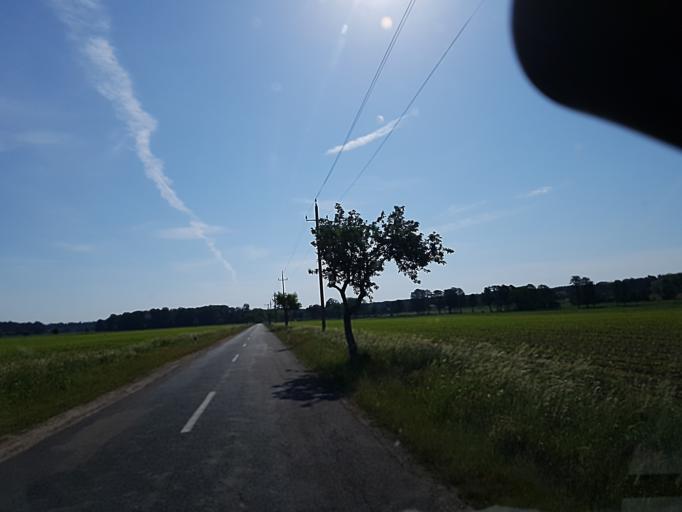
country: DE
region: Saxony-Anhalt
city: Rosslau
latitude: 52.0353
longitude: 12.2736
